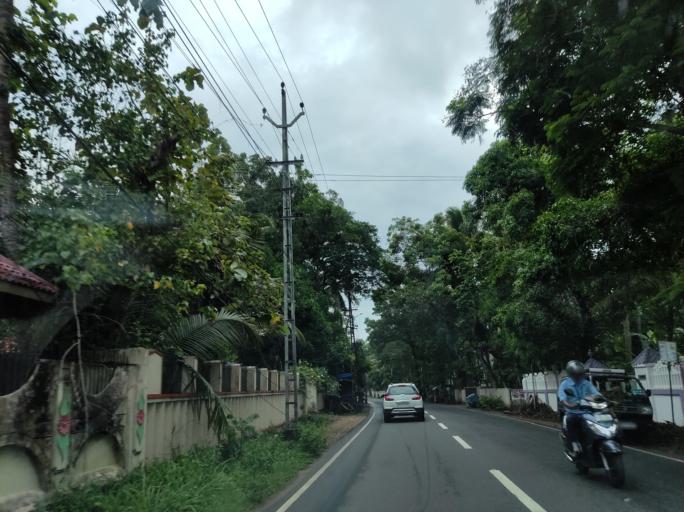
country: IN
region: Kerala
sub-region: Alappuzha
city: Mavelikara
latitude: 9.2519
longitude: 76.5119
